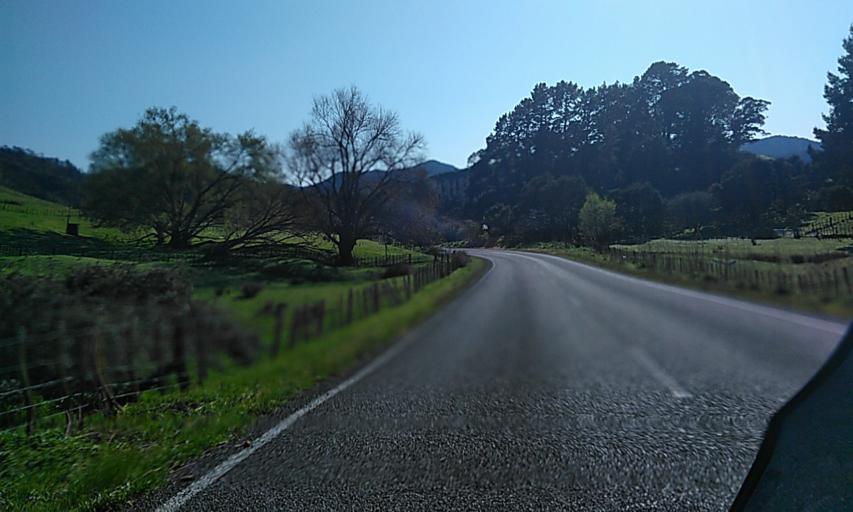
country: NZ
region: Gisborne
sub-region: Gisborne District
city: Gisborne
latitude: -38.5678
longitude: 178.0225
